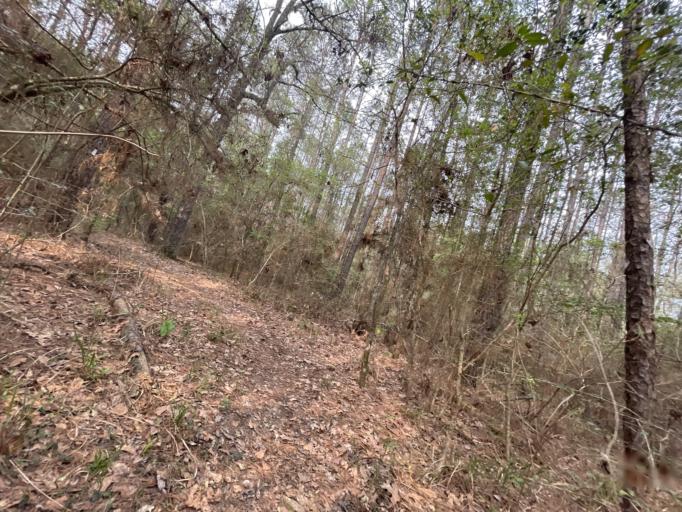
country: US
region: Texas
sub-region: Walker County
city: Huntsville
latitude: 30.6612
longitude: -95.4891
